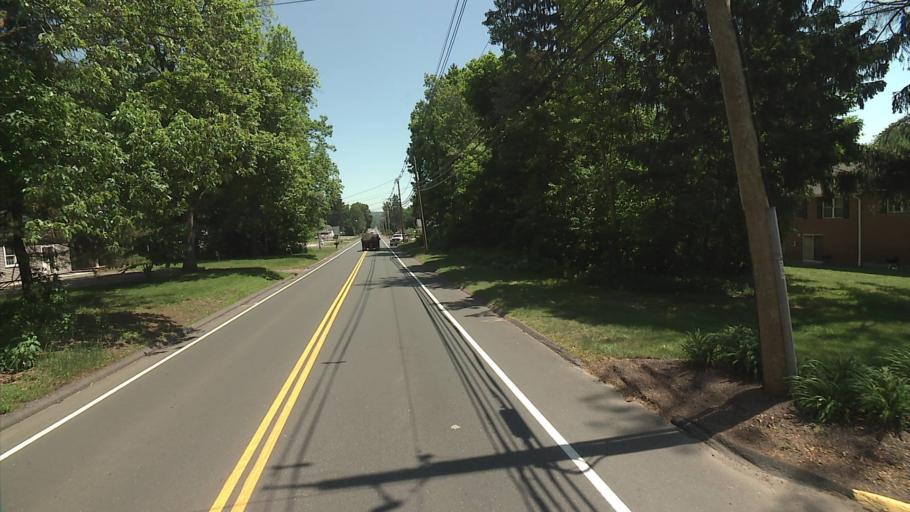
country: US
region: Connecticut
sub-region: Tolland County
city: Rockville
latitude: 41.8557
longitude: -72.4397
